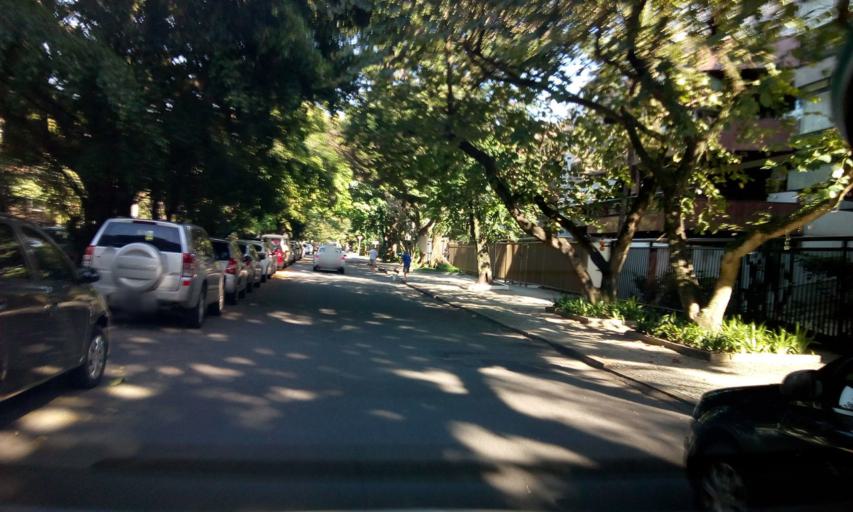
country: BR
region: Rio de Janeiro
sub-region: Rio De Janeiro
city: Rio de Janeiro
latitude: -23.0101
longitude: -43.3107
